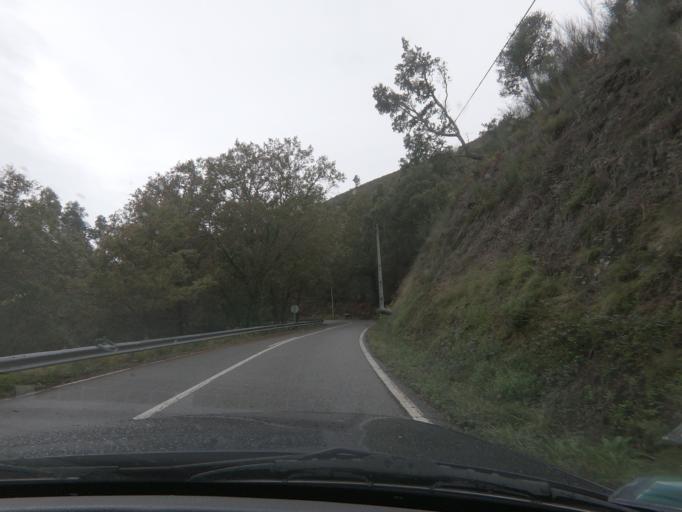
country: PT
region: Vila Real
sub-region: Mondim de Basto
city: Mondim de Basto
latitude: 41.3491
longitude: -7.8851
